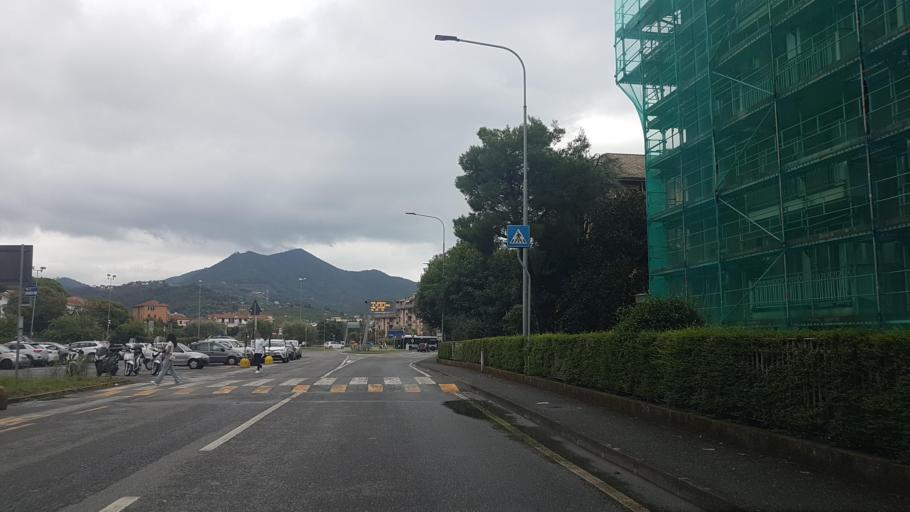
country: IT
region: Liguria
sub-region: Provincia di Genova
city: Sestri Levante
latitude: 44.2727
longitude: 9.4183
